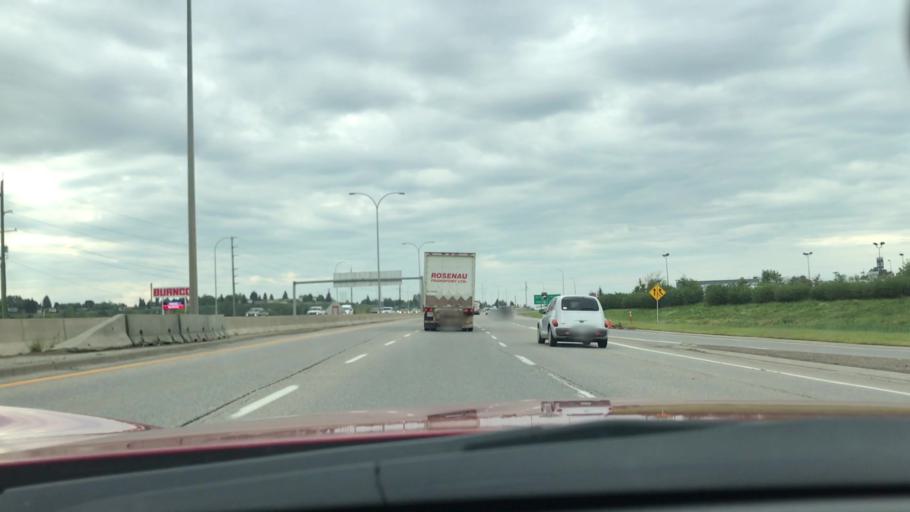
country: CA
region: Alberta
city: Calgary
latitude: 50.9916
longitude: -114.0315
